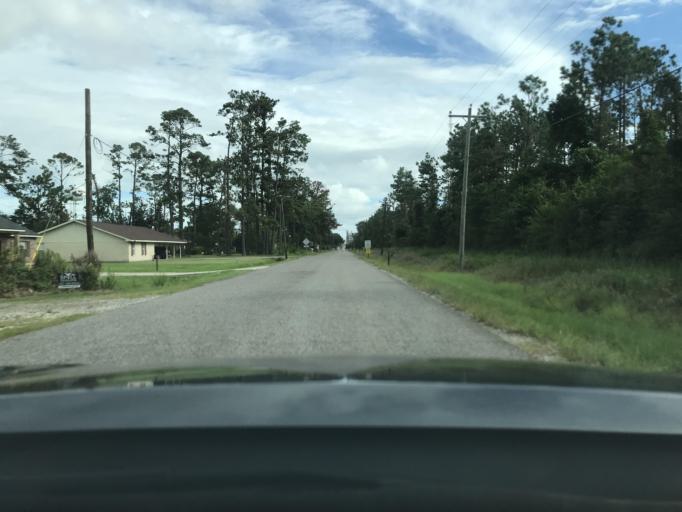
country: US
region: Louisiana
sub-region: Calcasieu Parish
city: Westlake
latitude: 30.2639
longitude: -93.2751
